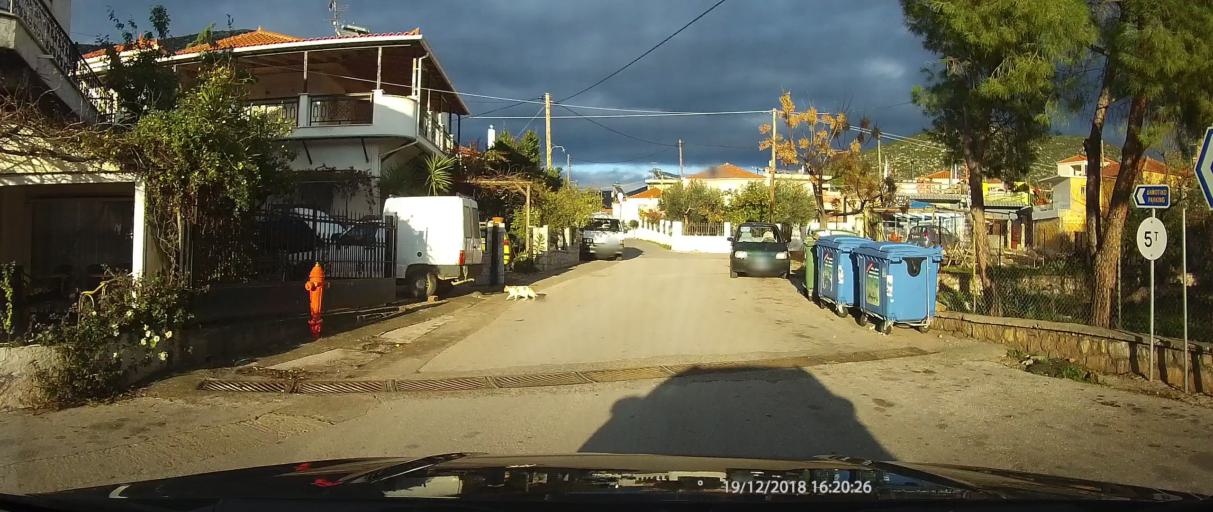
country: GR
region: Peloponnese
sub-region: Nomos Lakonias
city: Kato Glikovrisi
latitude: 36.9354
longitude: 22.8208
